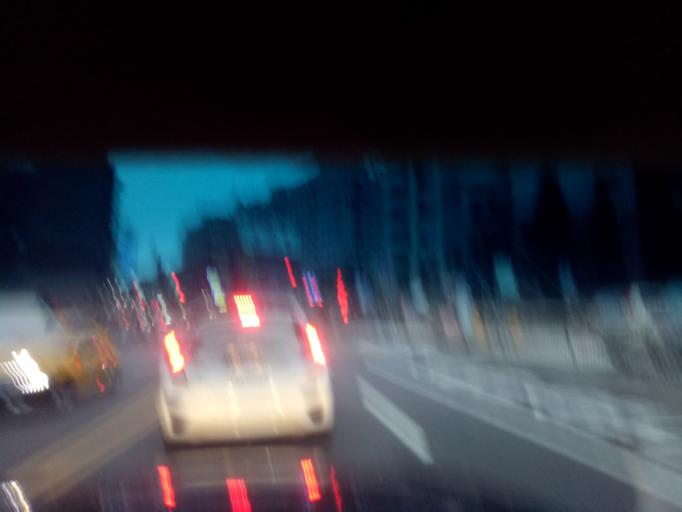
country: TW
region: Taiwan
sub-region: Keelung
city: Keelung
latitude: 25.1314
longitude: 121.7818
